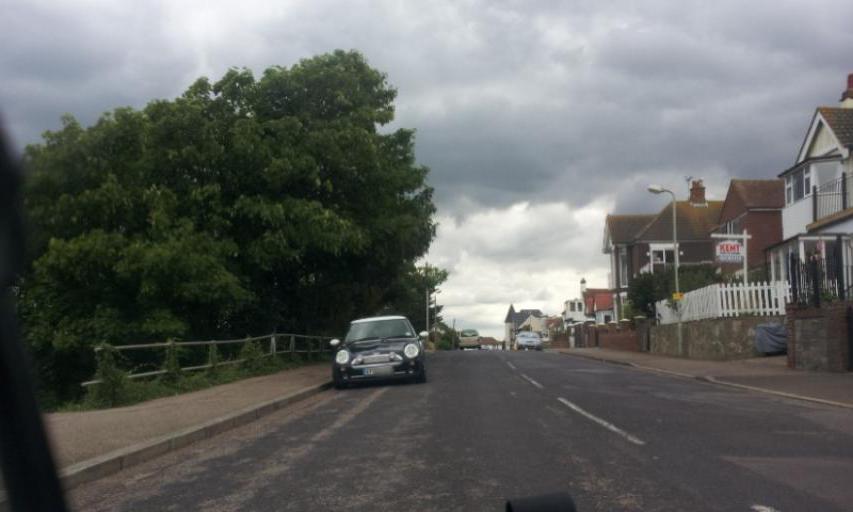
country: GB
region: England
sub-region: Kent
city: Herne Bay
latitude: 51.3716
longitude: 1.1021
